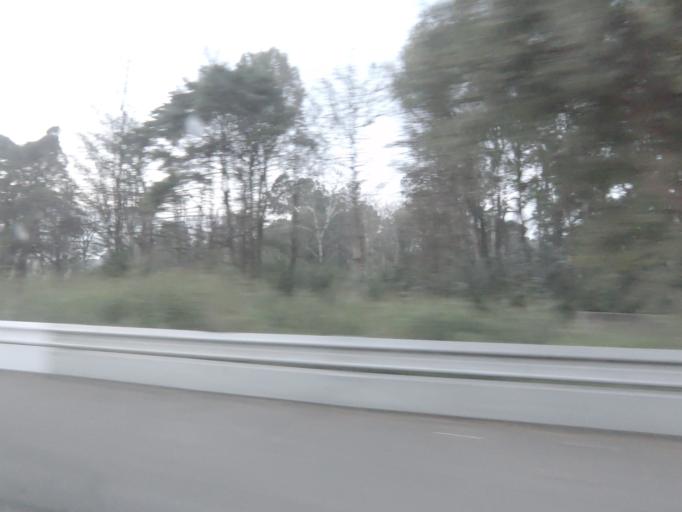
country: PT
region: Porto
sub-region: Matosinhos
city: Senhora da Hora
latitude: 41.1728
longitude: -8.6285
